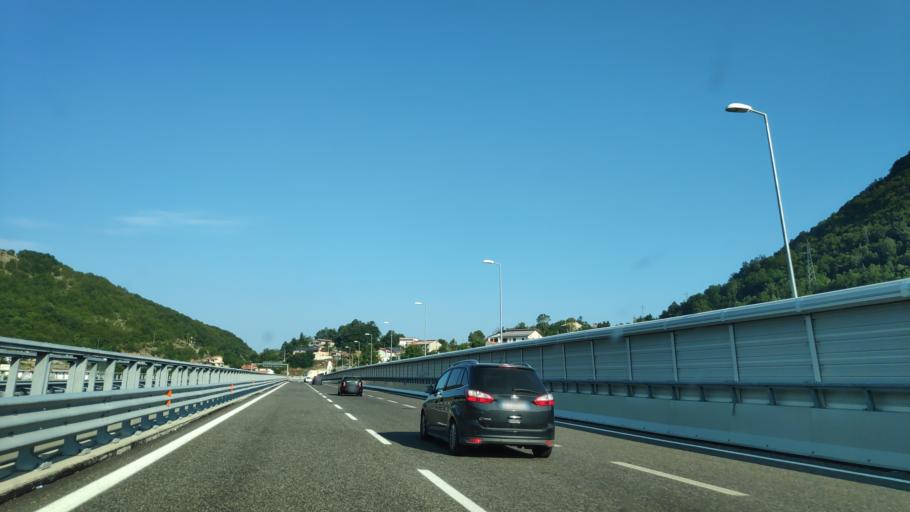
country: IT
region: Basilicate
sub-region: Provincia di Potenza
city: Lauria
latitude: 40.0190
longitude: 15.8857
